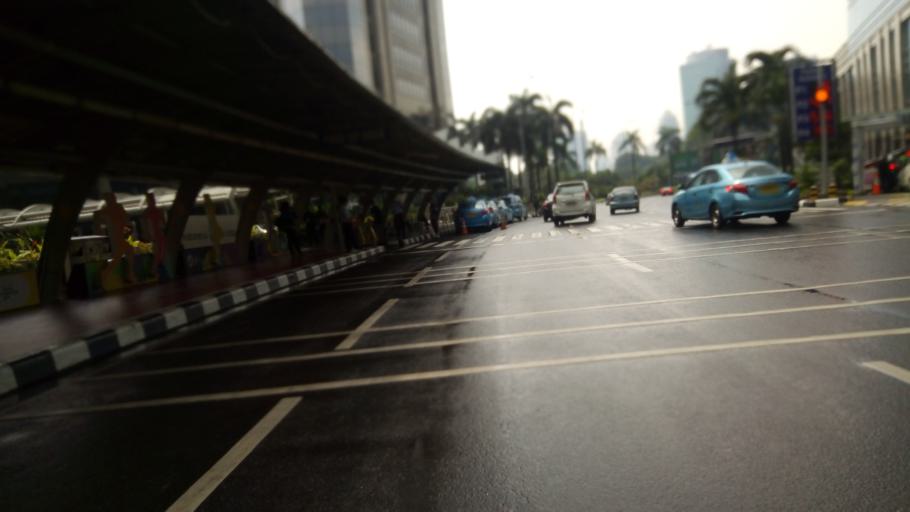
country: ID
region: Jakarta Raya
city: Jakarta
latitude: -6.2244
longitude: 106.8092
